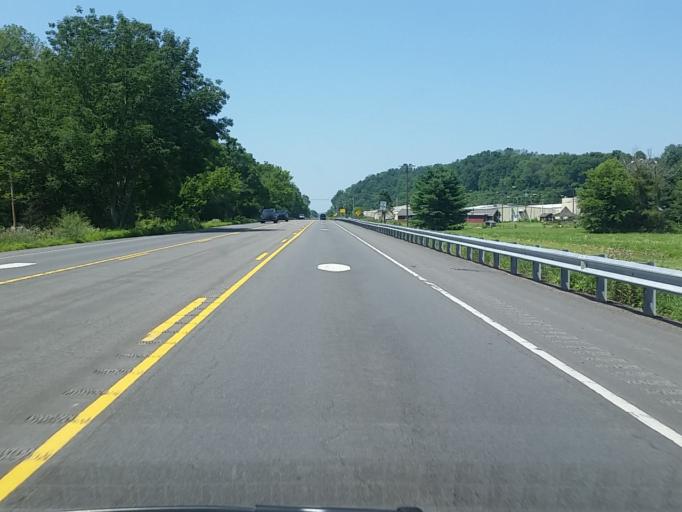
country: US
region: Pennsylvania
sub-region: Columbia County
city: Almedia
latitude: 41.0237
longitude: -76.3696
